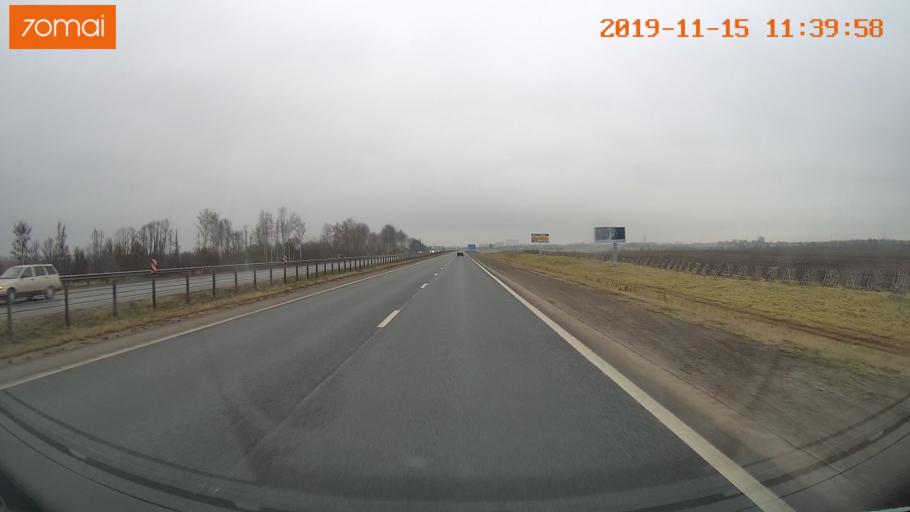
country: RU
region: Vologda
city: Molochnoye
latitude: 59.2121
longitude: 39.7390
